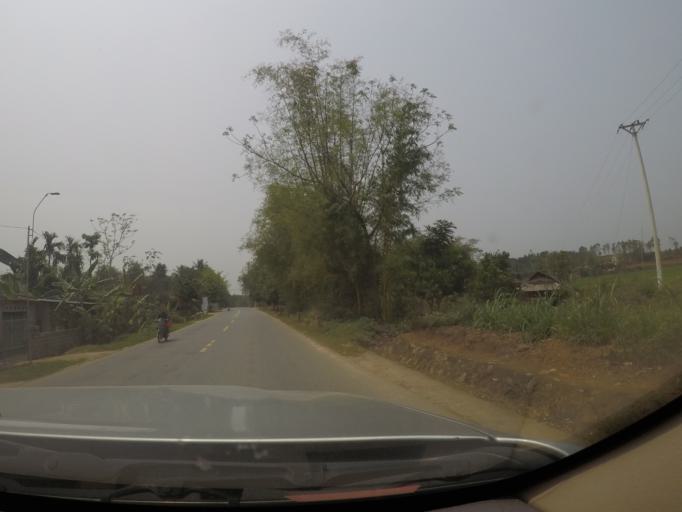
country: VN
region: Thanh Hoa
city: Thi Tran Ngoc Lac
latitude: 20.1393
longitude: 105.4227
